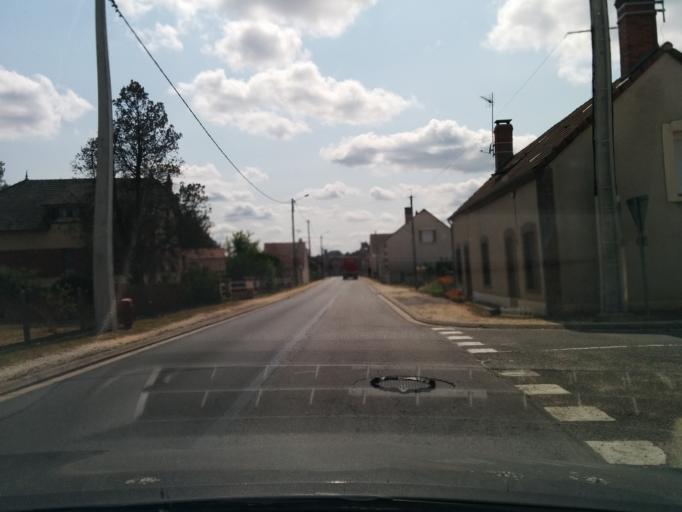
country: FR
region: Centre
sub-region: Departement du Cher
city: Neuvy-sur-Barangeon
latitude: 47.3165
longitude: 2.2578
